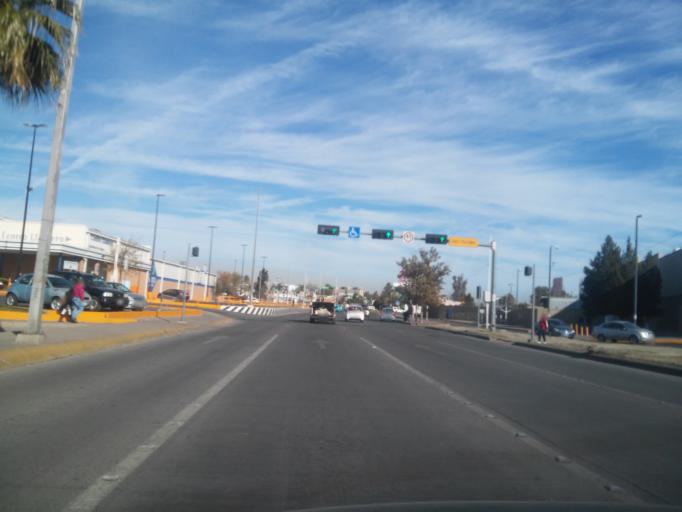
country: MX
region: Durango
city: Victoria de Durango
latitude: 24.0357
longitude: -104.6543
